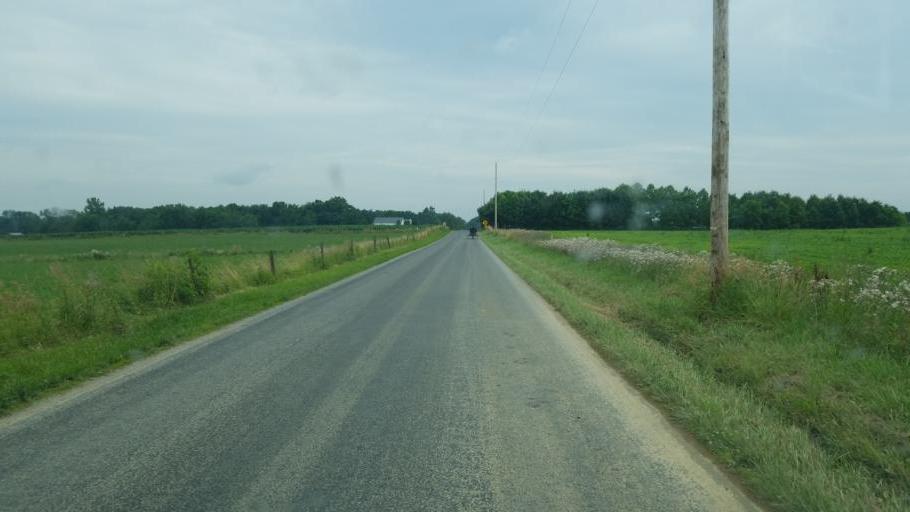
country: US
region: Ohio
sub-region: Wayne County
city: Orrville
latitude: 40.7810
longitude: -81.7753
